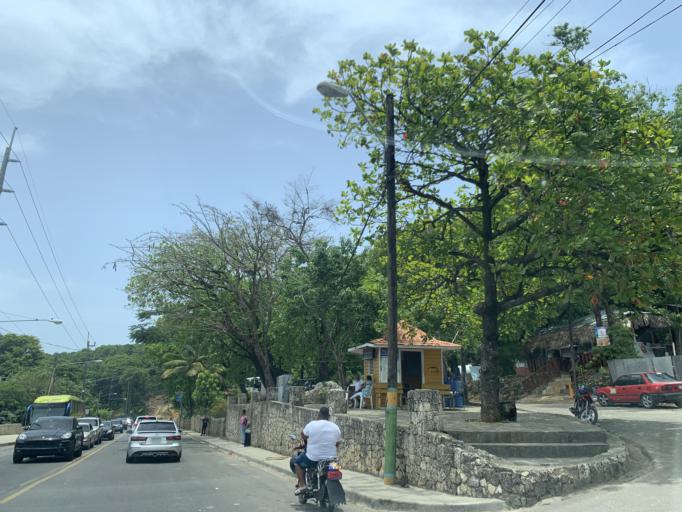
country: DO
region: Puerto Plata
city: Cabarete
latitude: 19.7527
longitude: -70.5189
